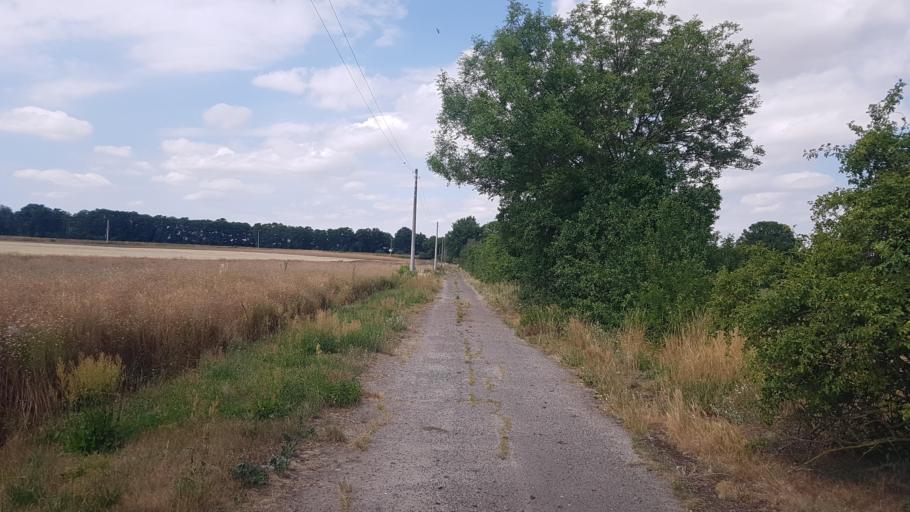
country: DE
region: Brandenburg
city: Juterbog
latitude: 51.9631
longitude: 13.0399
